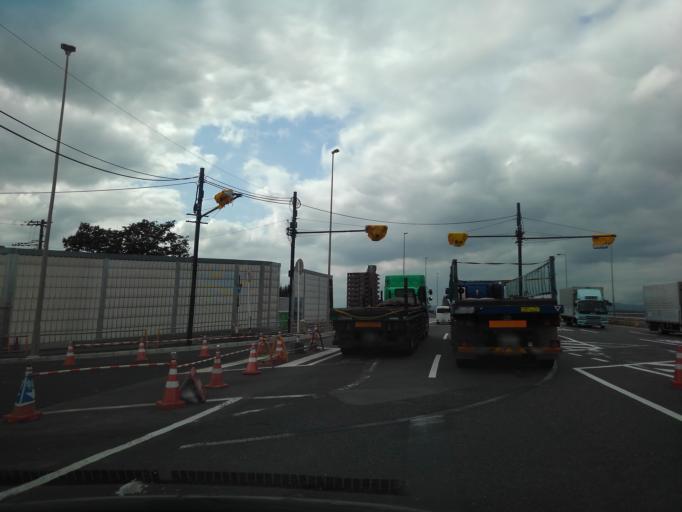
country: JP
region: Tokyo
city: Fussa
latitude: 35.7238
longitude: 139.3434
